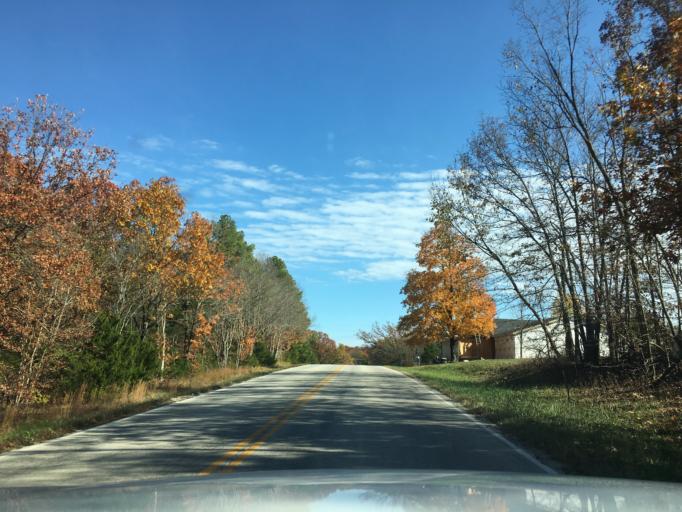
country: US
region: Missouri
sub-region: Maries County
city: Belle
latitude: 38.3123
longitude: -91.7451
